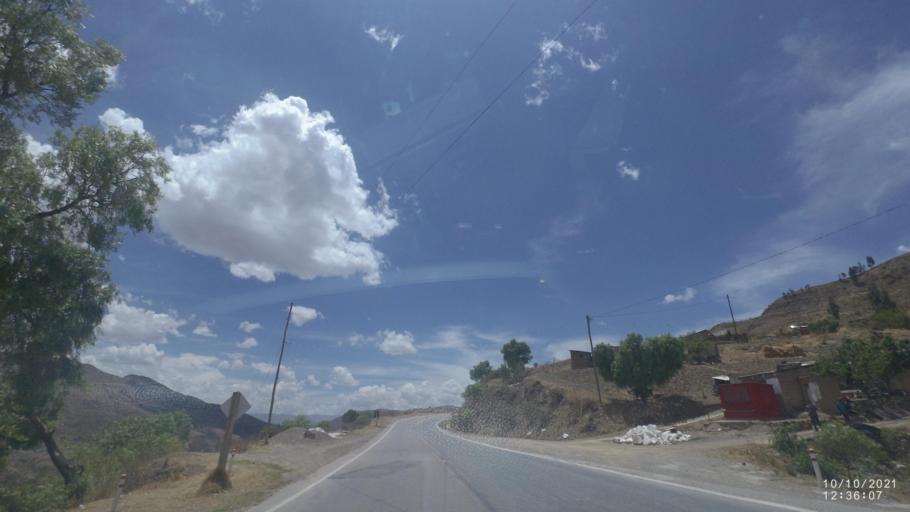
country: BO
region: Cochabamba
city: Irpa Irpa
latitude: -17.6625
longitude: -66.4061
